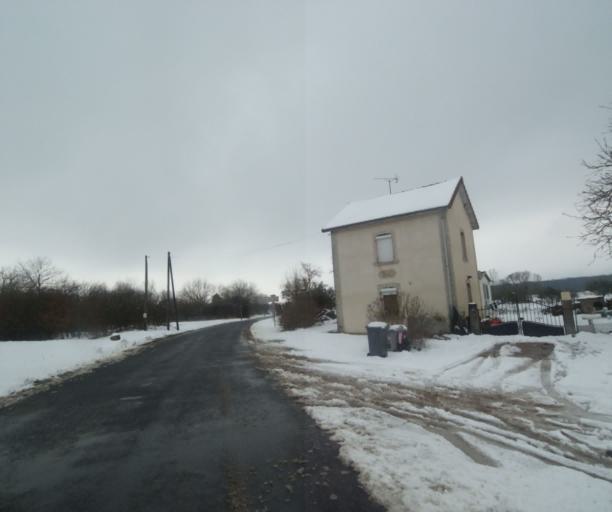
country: FR
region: Champagne-Ardenne
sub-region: Departement de la Haute-Marne
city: Montier-en-Der
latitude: 48.4722
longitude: 4.7883
